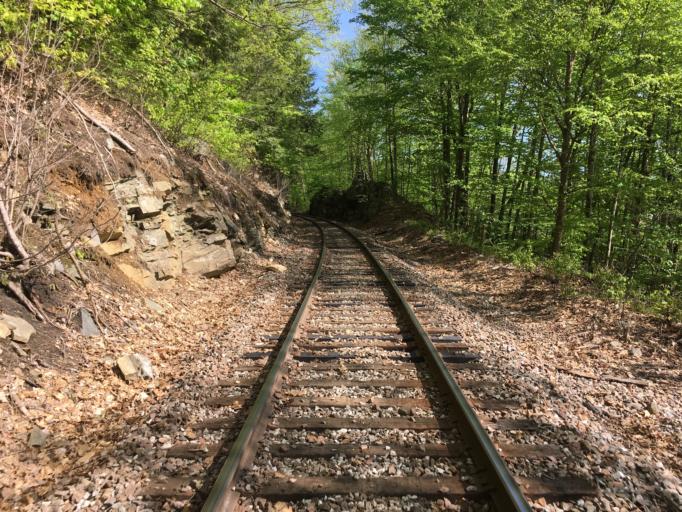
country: US
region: Vermont
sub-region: Windsor County
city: Chester
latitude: 43.3222
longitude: -72.6079
